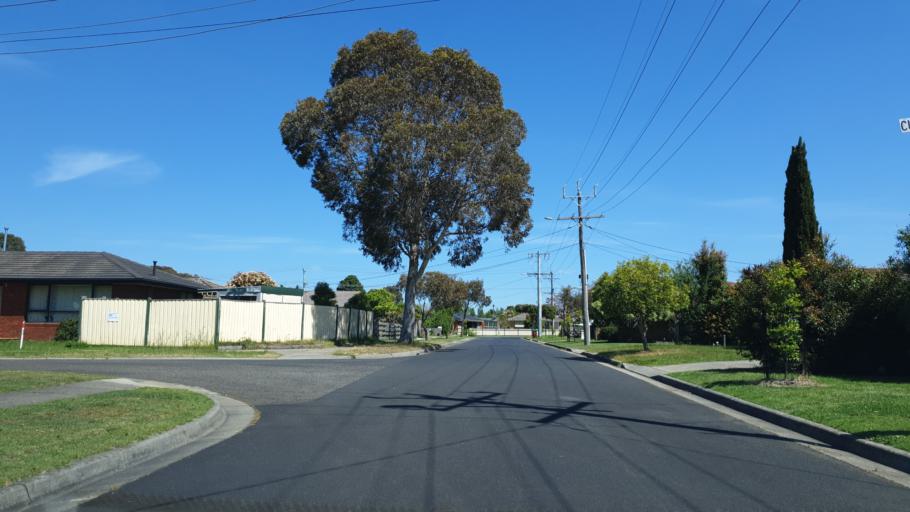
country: AU
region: Victoria
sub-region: Casey
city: Cranbourne North
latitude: -38.0918
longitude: 145.2756
